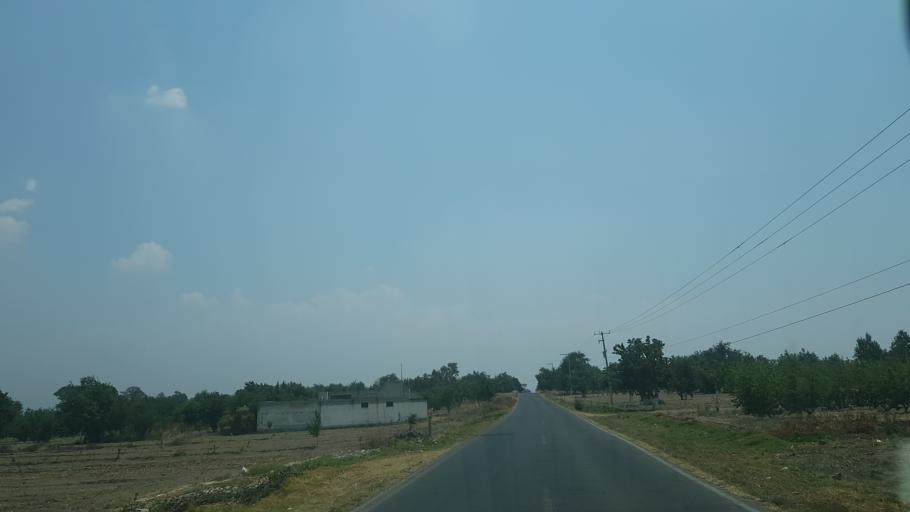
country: MX
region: Puebla
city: San Andres Calpan
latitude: 19.0984
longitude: -98.4248
